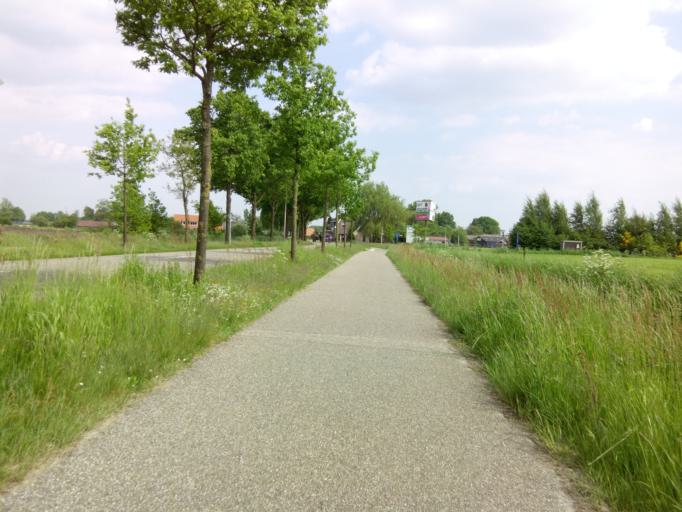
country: NL
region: Gelderland
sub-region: Oost Gelre
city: Lichtenvoorde
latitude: 52.0561
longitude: 6.5774
